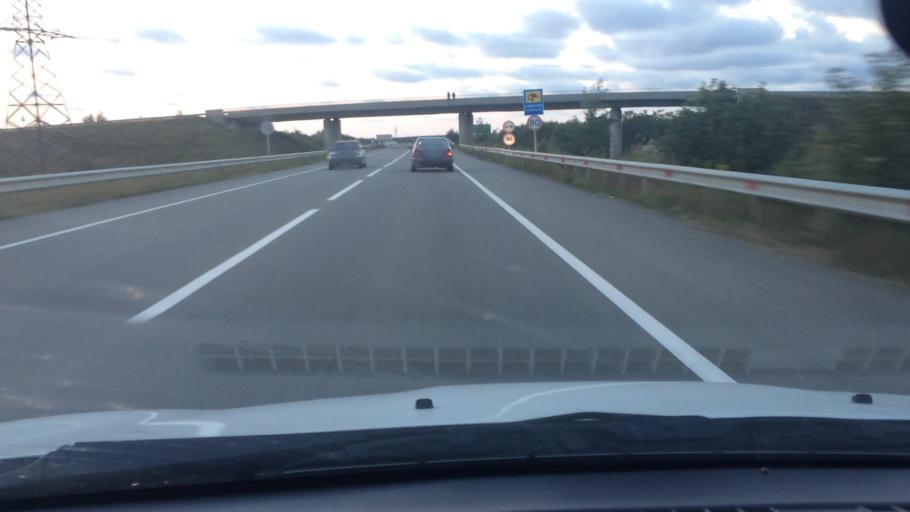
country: GE
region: Ajaria
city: Ochkhamuri
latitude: 41.8916
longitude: 41.8060
